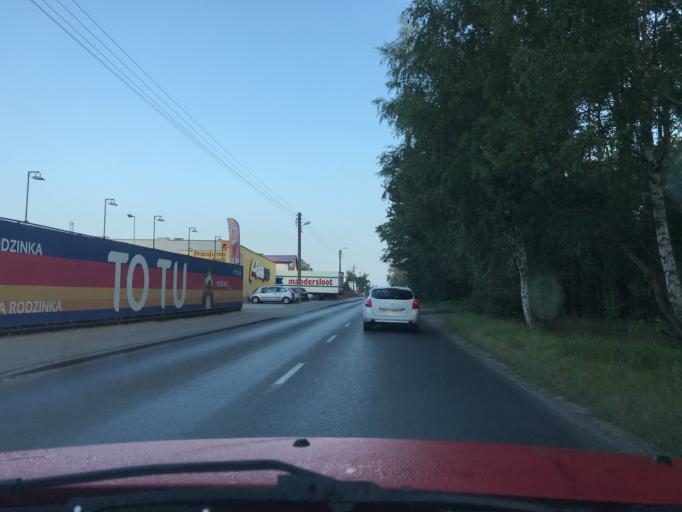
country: PL
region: Greater Poland Voivodeship
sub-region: Powiat poznanski
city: Plewiska
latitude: 52.3989
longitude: 16.8013
